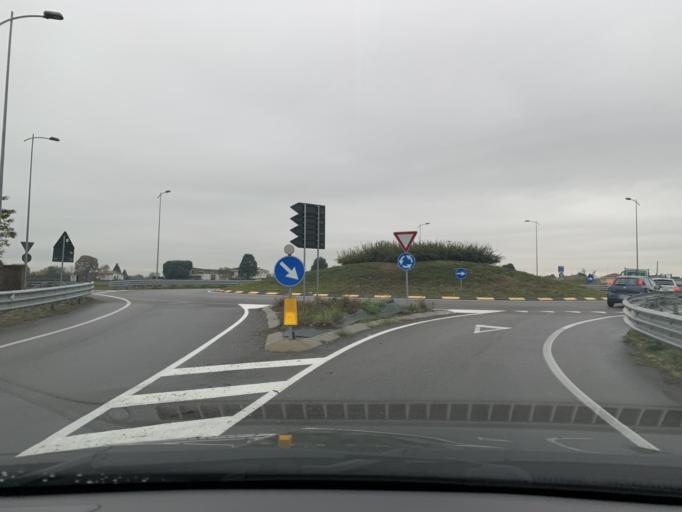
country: IT
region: Lombardy
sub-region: Provincia di Como
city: Rovello Porro
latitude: 45.6523
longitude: 9.0524
